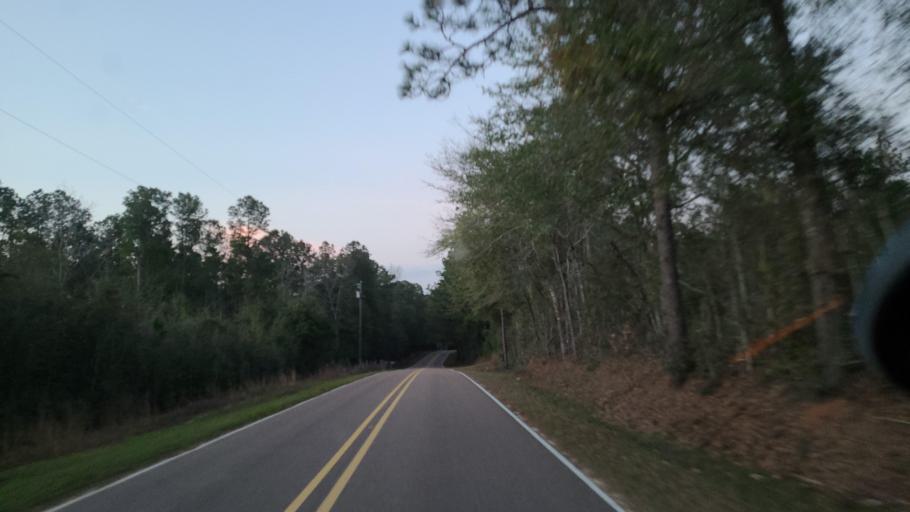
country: US
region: Mississippi
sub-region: Forrest County
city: Hattiesburg
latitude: 31.2365
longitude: -89.2420
